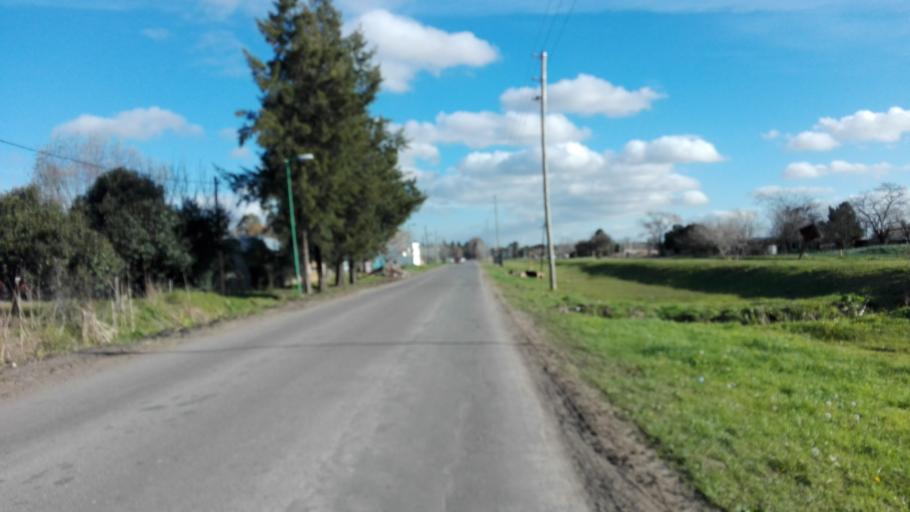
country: AR
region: Buenos Aires
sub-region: Partido de La Plata
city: La Plata
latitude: -34.9103
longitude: -58.0211
